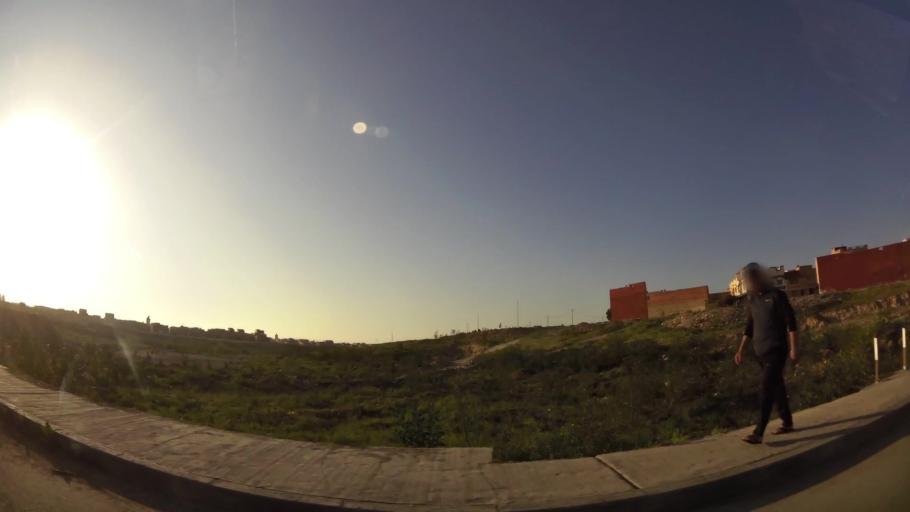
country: MA
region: Oriental
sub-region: Oujda-Angad
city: Oujda
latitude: 34.7050
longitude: -1.9026
